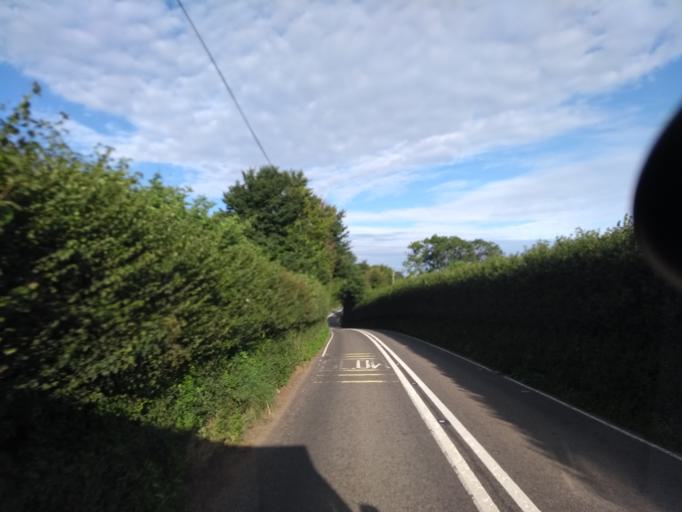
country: GB
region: England
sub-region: Somerset
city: Williton
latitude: 51.1770
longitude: -3.2341
